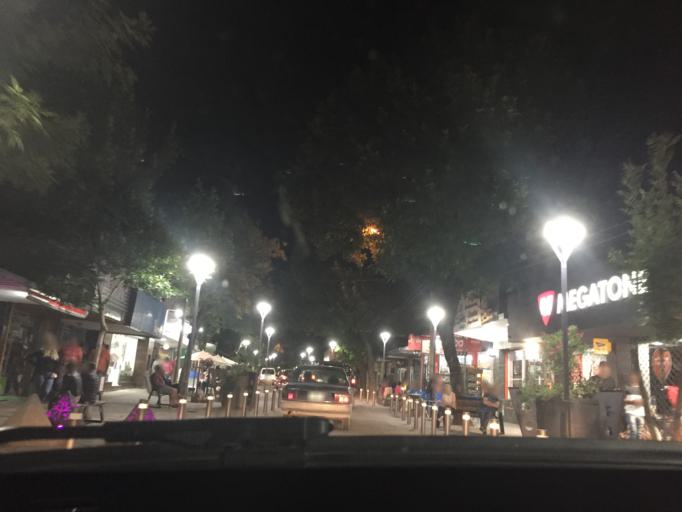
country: AR
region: Cordoba
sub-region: Departamento de Calamuchita
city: Santa Rosa de Calamuchita
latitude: -32.0688
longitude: -64.5373
